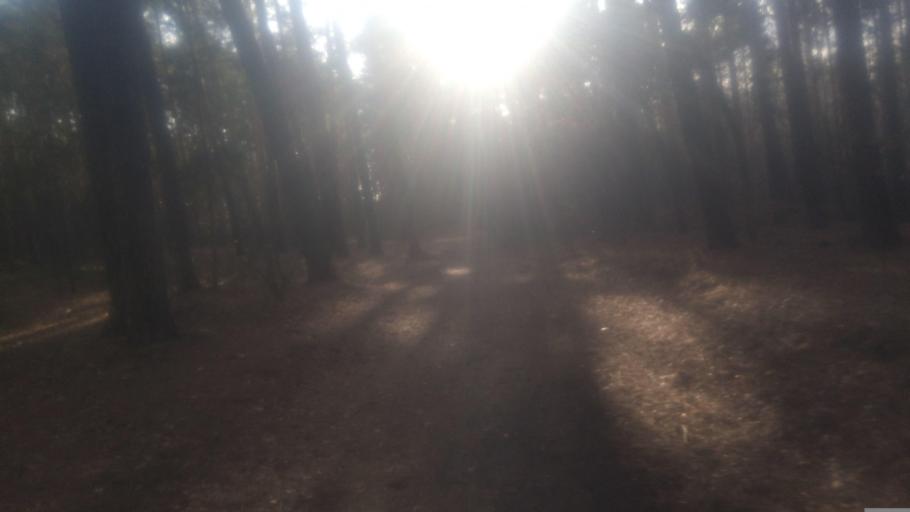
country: RU
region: Chelyabinsk
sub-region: Gorod Chelyabinsk
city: Chelyabinsk
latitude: 55.1665
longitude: 61.3367
